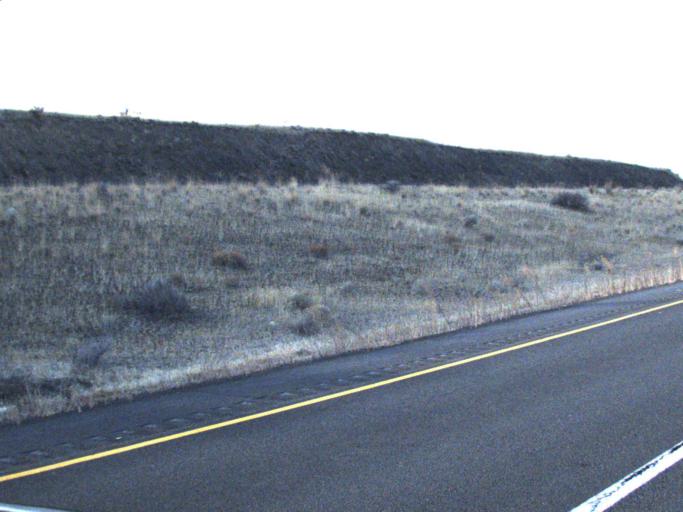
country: US
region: Washington
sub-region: Adams County
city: Ritzville
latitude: 46.9952
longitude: -118.5480
